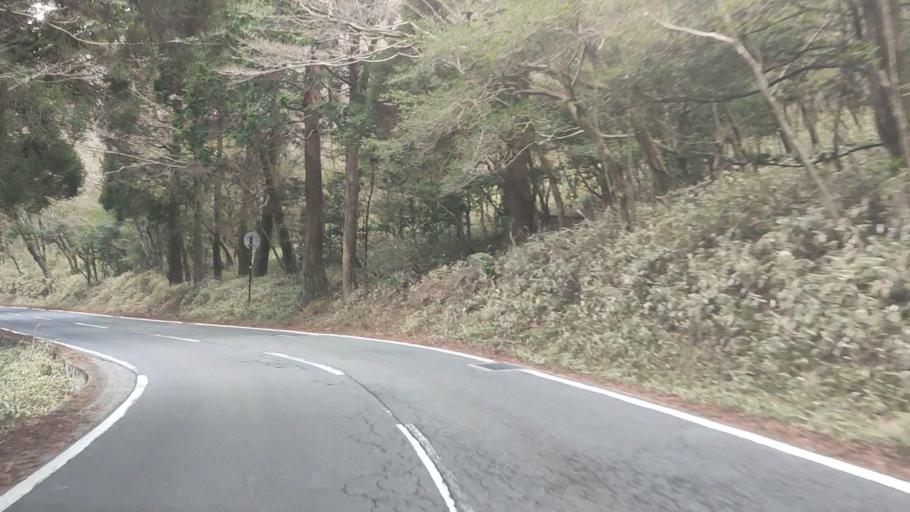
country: JP
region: Nagasaki
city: Shimabara
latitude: 32.7542
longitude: 130.2739
